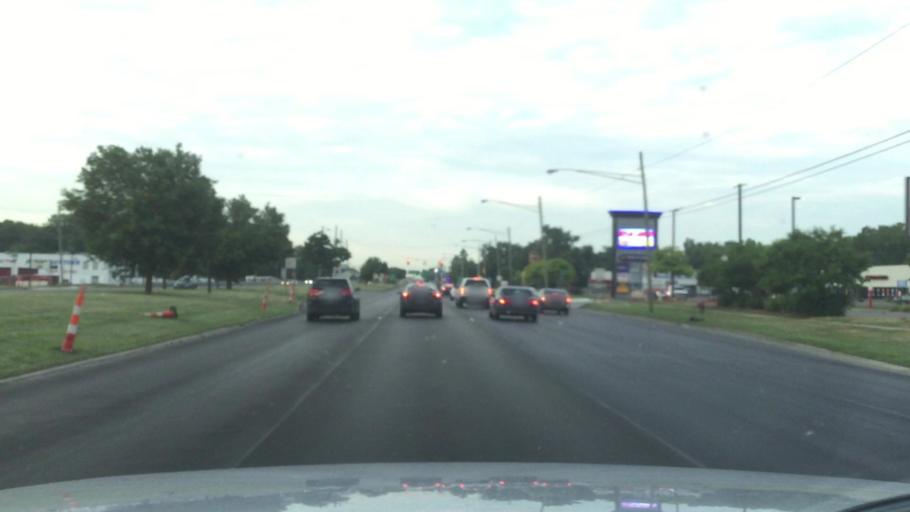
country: US
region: Michigan
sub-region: Wayne County
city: Redford
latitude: 42.3962
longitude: -83.2767
